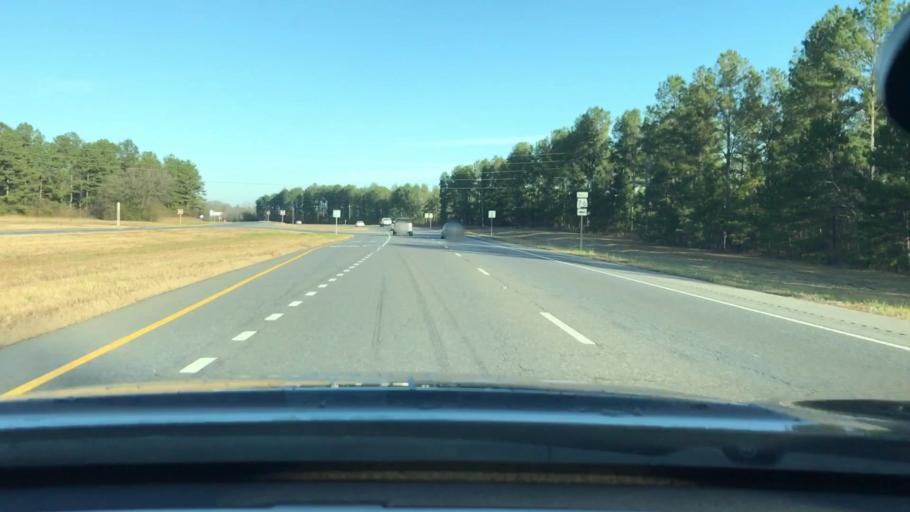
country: US
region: Alabama
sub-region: Talladega County
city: Childersburg
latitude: 33.2991
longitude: -86.3688
